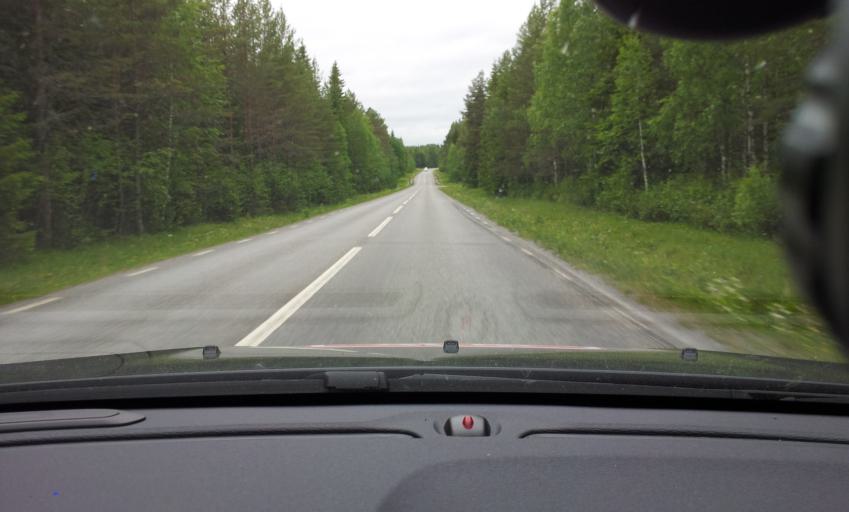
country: SE
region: Jaemtland
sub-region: Krokoms Kommun
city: Krokom
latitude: 63.1284
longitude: 14.2292
